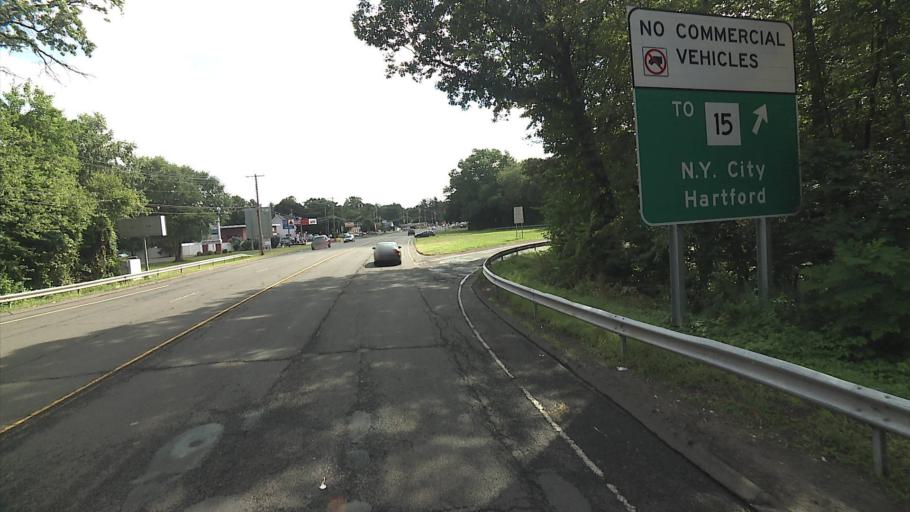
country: US
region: Connecticut
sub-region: New Haven County
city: City of Milford (balance)
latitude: 41.2317
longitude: -73.0616
